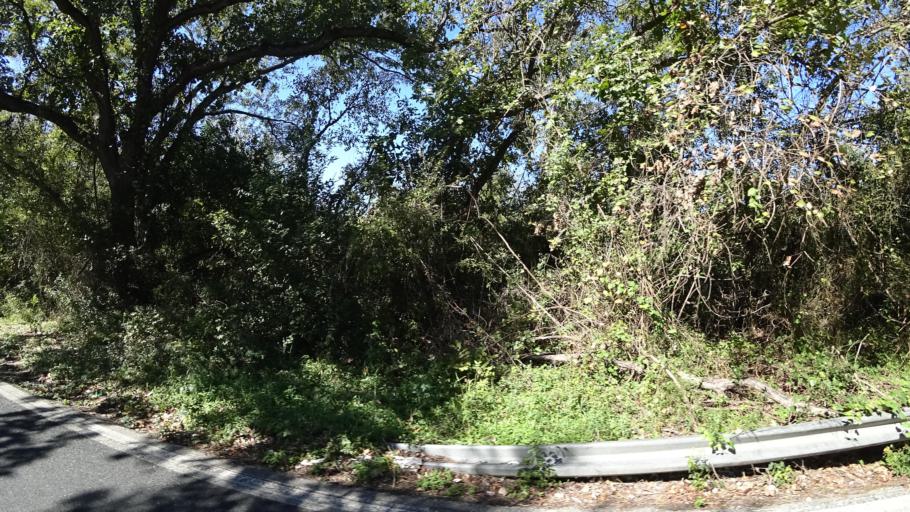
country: US
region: Texas
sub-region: Travis County
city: Hornsby Bend
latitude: 30.2837
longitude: -97.6527
